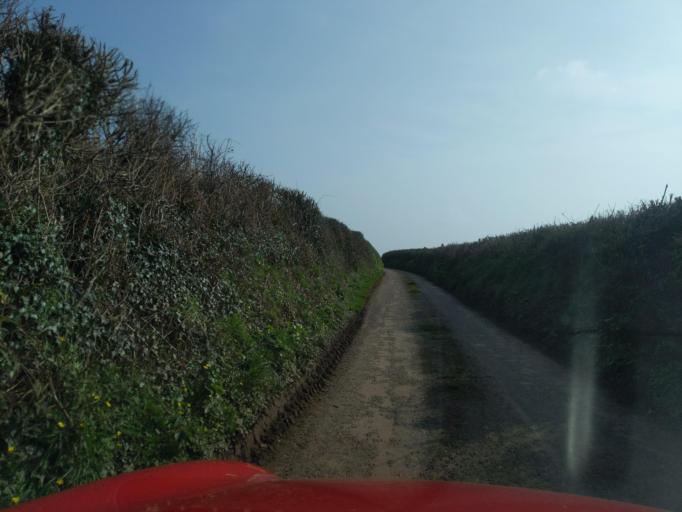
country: GB
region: England
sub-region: Devon
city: Kingsbridge
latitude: 50.2883
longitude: -3.7340
